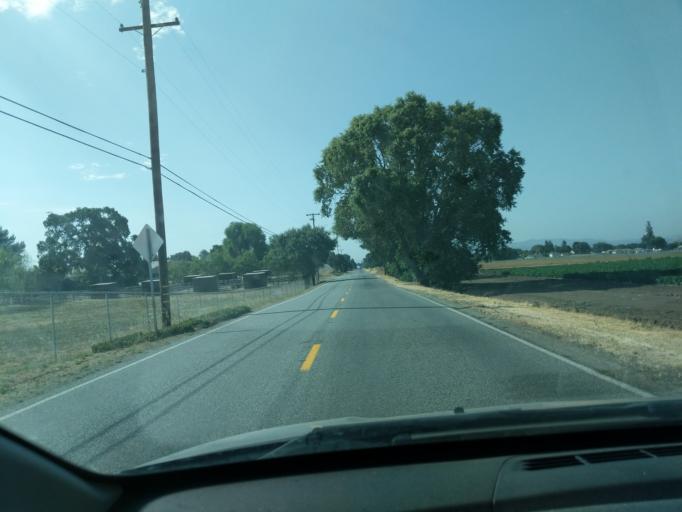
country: US
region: California
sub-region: Santa Clara County
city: Gilroy
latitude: 37.0468
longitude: -121.5448
